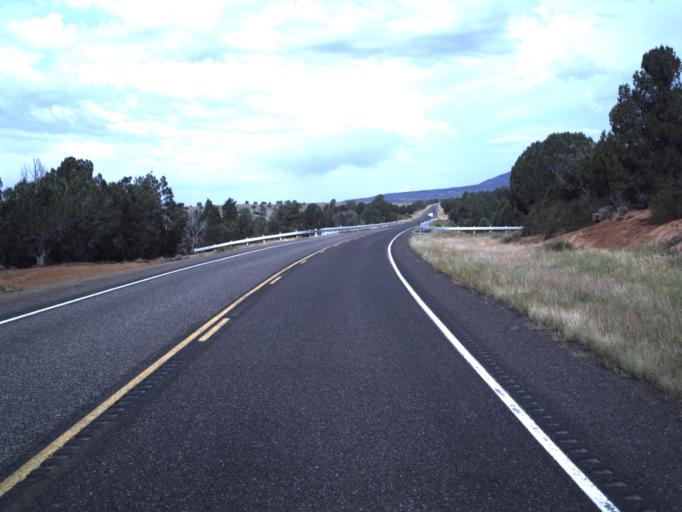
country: US
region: Utah
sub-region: Kane County
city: Kanab
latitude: 37.2210
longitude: -112.7114
